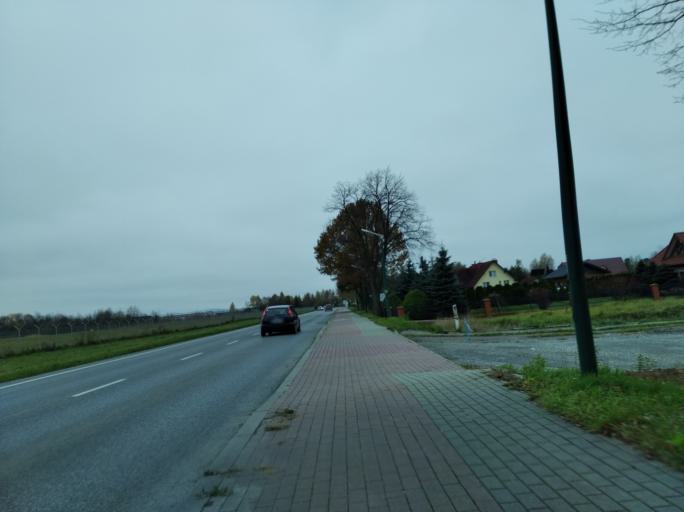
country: PL
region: Subcarpathian Voivodeship
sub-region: Krosno
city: Krosno
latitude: 49.6846
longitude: 21.7237
